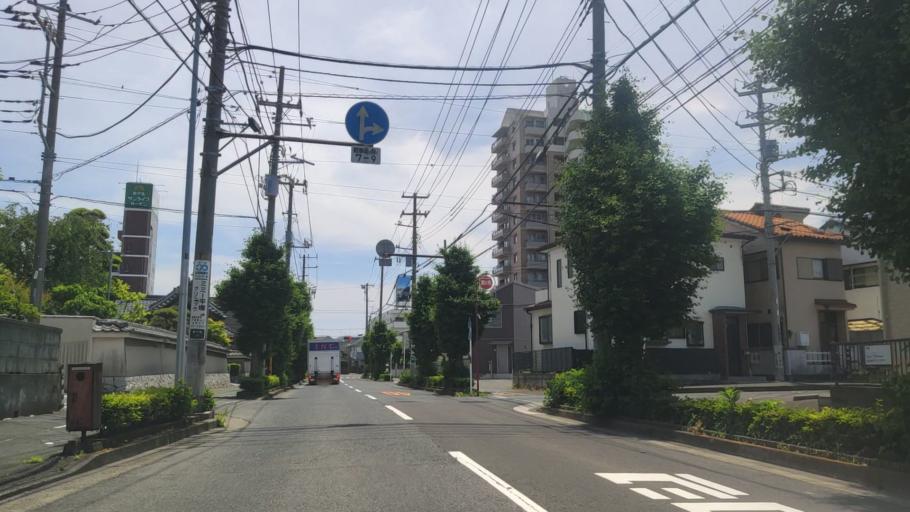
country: JP
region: Kanagawa
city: Hiratsuka
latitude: 35.3328
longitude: 139.3626
